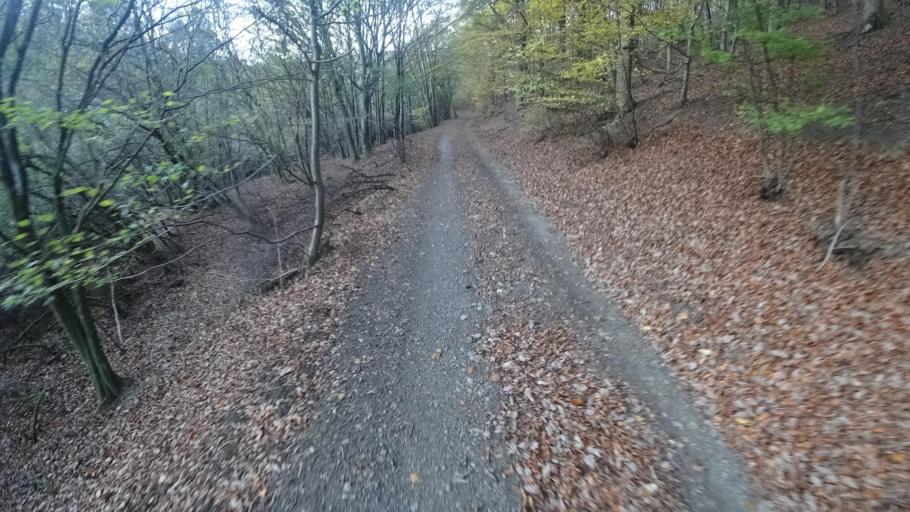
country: DE
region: Rheinland-Pfalz
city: Berg
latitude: 50.5330
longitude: 6.9565
